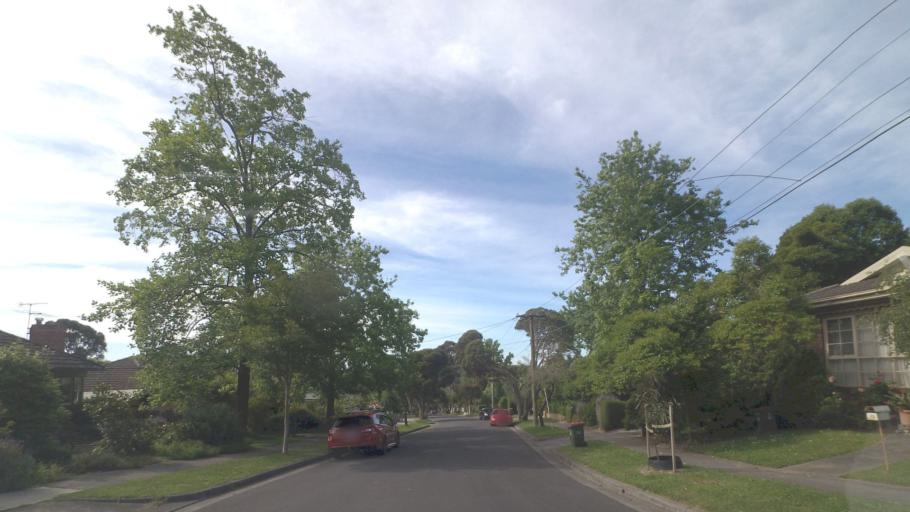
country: AU
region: Victoria
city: Mitcham
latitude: -37.8137
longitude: 145.1983
